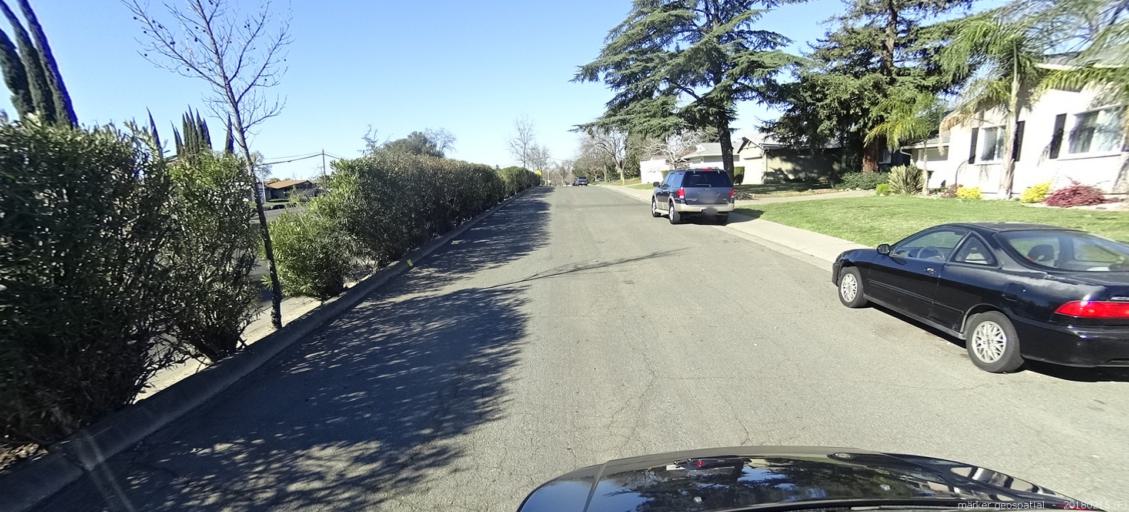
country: US
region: California
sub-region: Sacramento County
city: Foothill Farms
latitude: 38.6637
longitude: -121.3159
